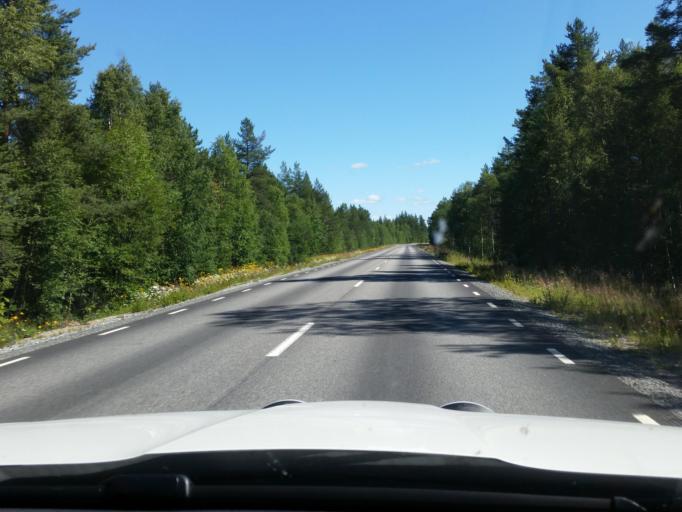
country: SE
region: Norrbotten
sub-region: Pitea Kommun
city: Roknas
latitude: 65.3419
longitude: 20.9441
